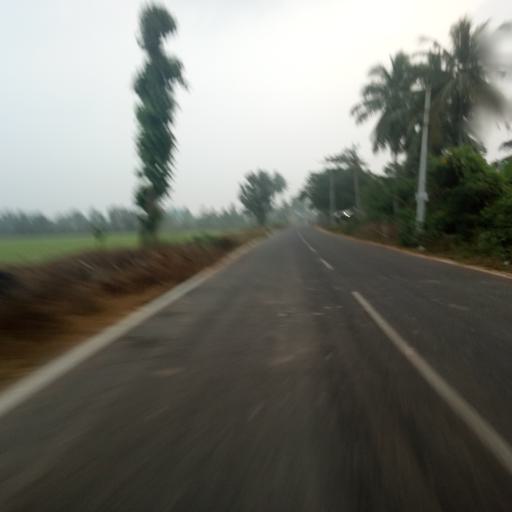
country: IN
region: Andhra Pradesh
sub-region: Nellore
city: Nellore
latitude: 14.4431
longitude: 80.1053
